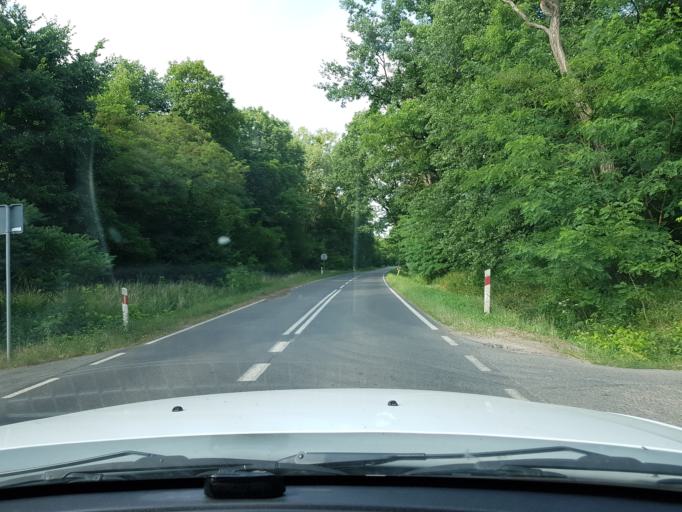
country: PL
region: West Pomeranian Voivodeship
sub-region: Powiat gryfinski
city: Moryn
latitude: 52.9222
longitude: 14.3669
